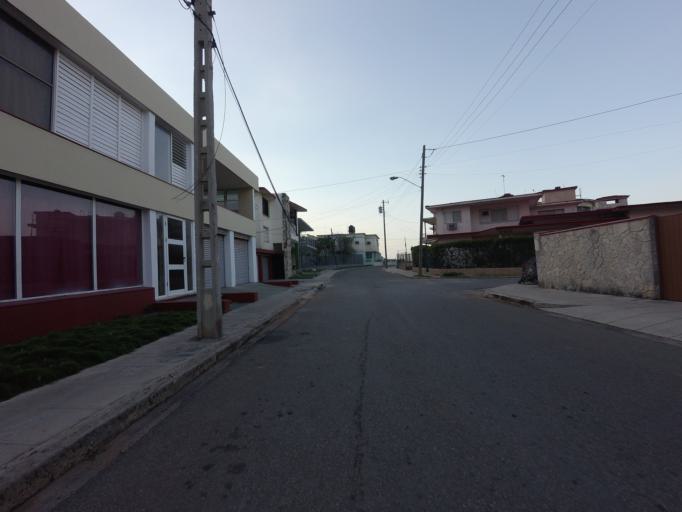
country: CU
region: La Habana
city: Cerro
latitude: 23.0949
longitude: -82.4609
